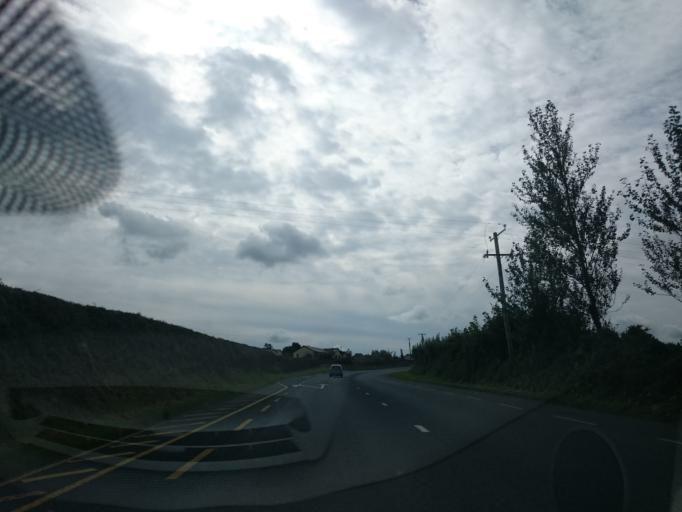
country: IE
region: Munster
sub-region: Waterford
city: Tra Mhor
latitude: 52.2239
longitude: -7.1996
